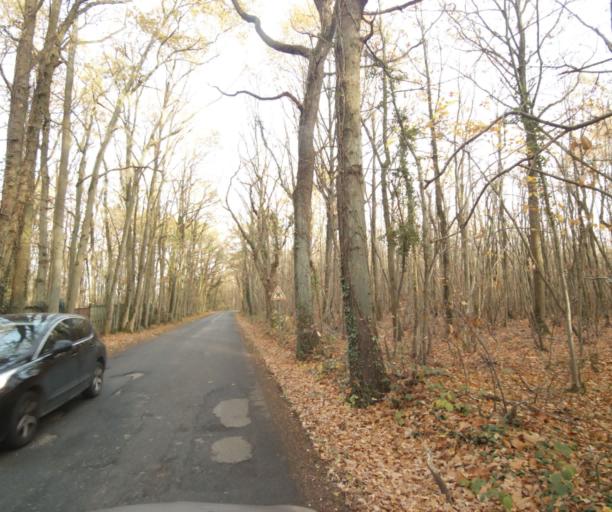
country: FR
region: Ile-de-France
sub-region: Departement des Yvelines
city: Chanteloup-les-Vignes
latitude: 48.9951
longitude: 2.0235
